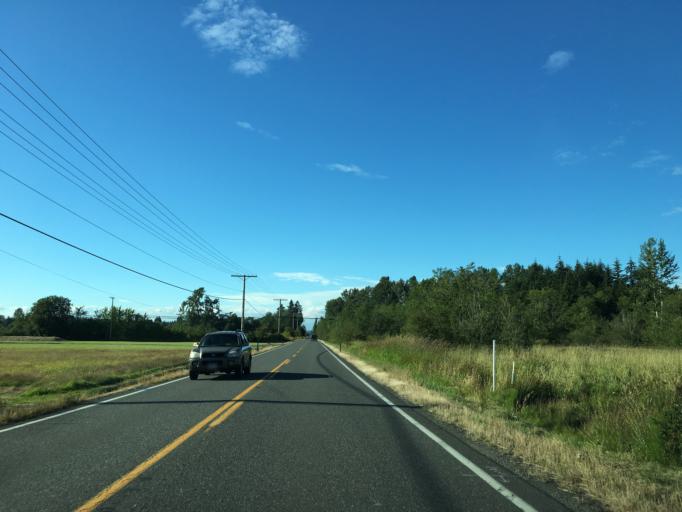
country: US
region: Washington
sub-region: Whatcom County
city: Birch Bay
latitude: 48.9088
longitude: -122.7266
